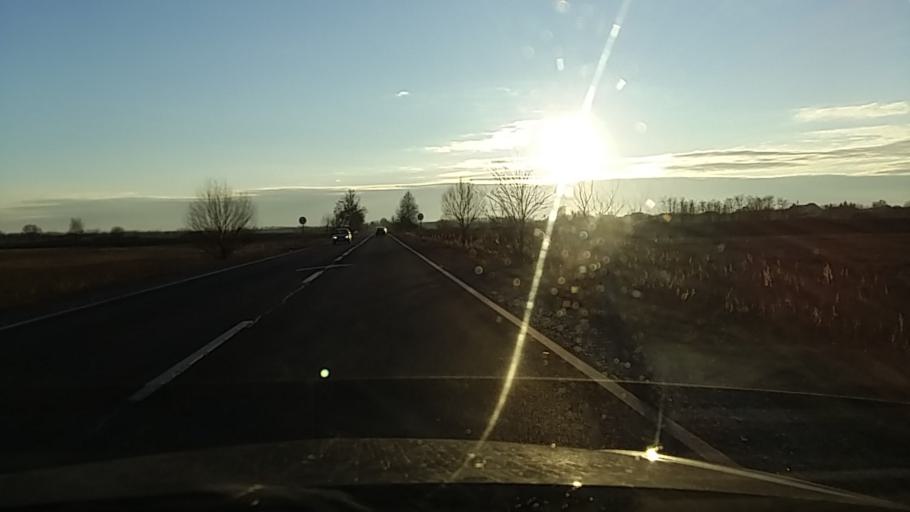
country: HU
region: Szabolcs-Szatmar-Bereg
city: Ujfeherto
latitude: 47.7808
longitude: 21.6869
